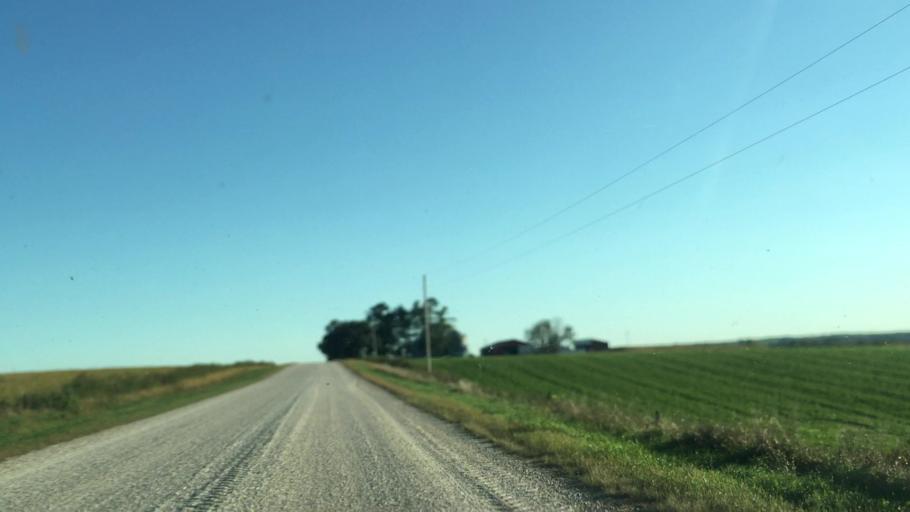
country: US
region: Minnesota
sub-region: Fillmore County
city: Preston
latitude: 43.8109
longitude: -92.0396
